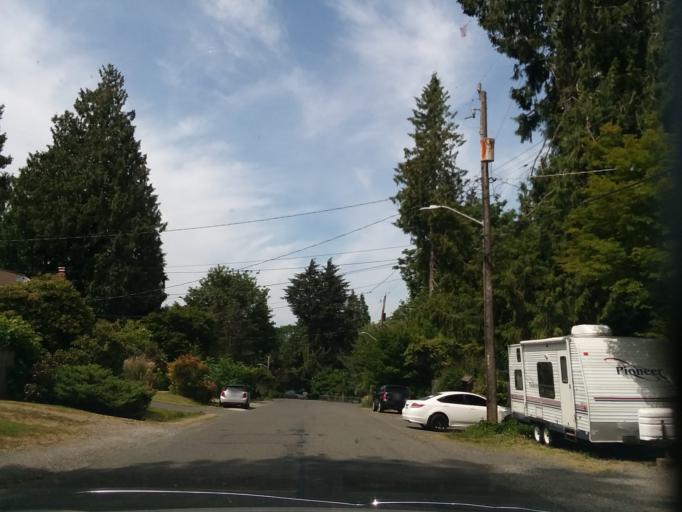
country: US
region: Washington
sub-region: King County
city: Lake Forest Park
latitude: 47.7207
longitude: -122.3091
